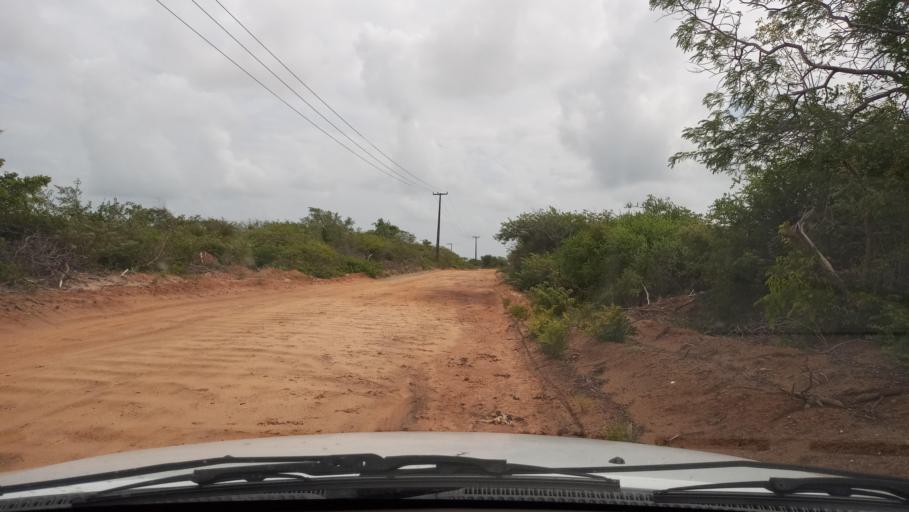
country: BR
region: Rio Grande do Norte
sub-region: Maxaranguape
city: Sao Miguel
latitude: -5.4713
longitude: -35.3003
